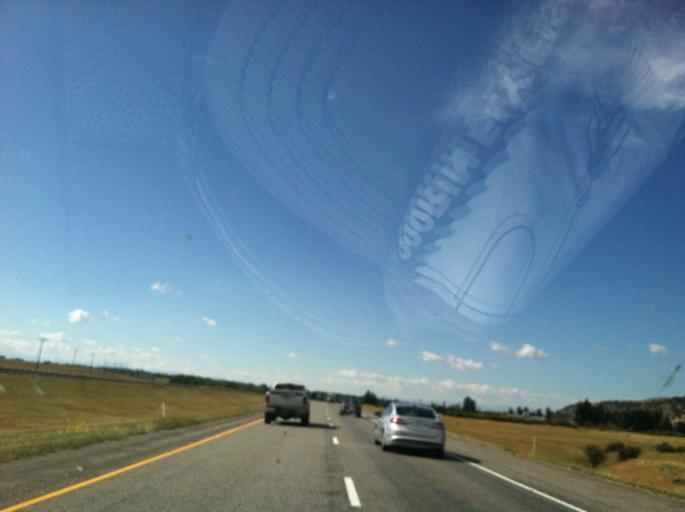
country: US
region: Montana
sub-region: Gallatin County
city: Bozeman
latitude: 45.6637
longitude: -110.9681
